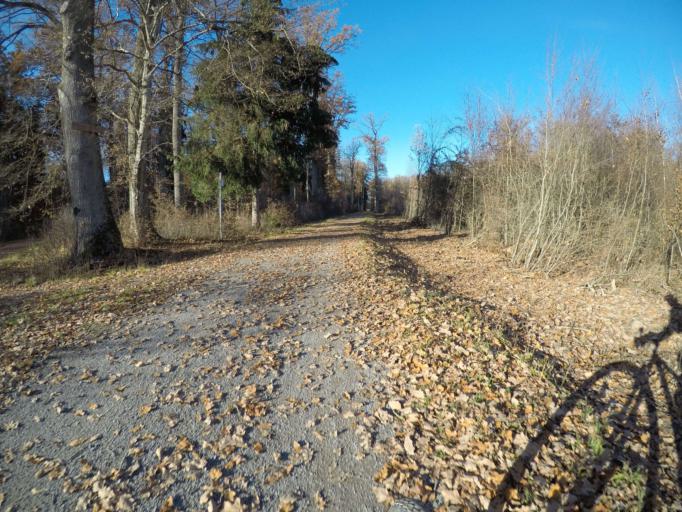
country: DE
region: Baden-Wuerttemberg
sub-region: Regierungsbezirk Stuttgart
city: Ehningen
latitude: 48.6782
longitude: 8.9596
